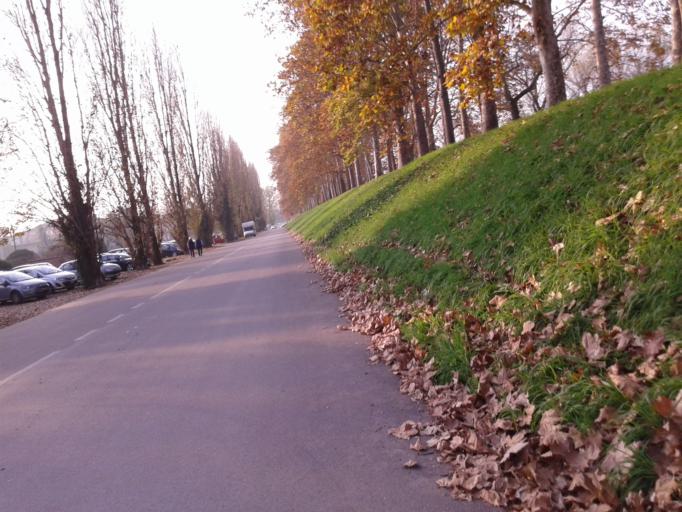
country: IT
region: Emilia-Romagna
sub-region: Provincia di Ferrara
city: Ferrara
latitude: 44.8491
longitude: 11.6240
